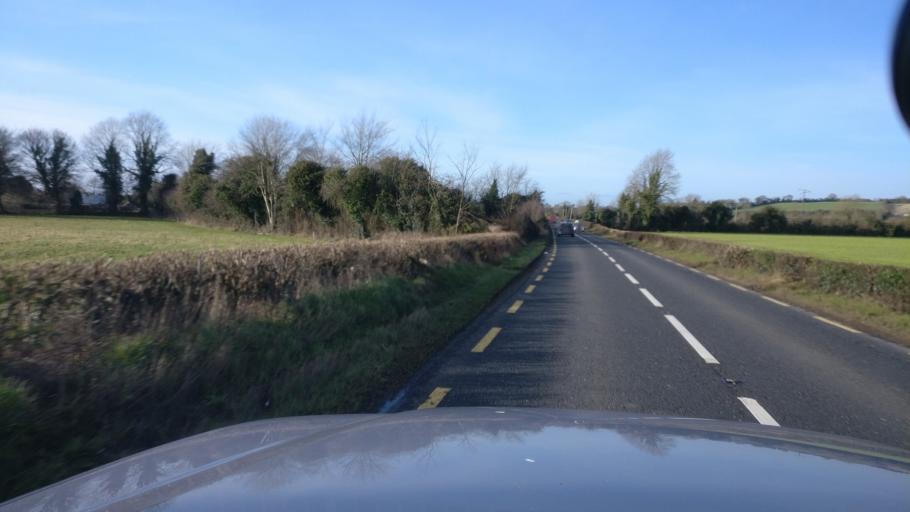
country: IE
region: Leinster
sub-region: Laois
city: Mountmellick
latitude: 53.1893
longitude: -7.4061
